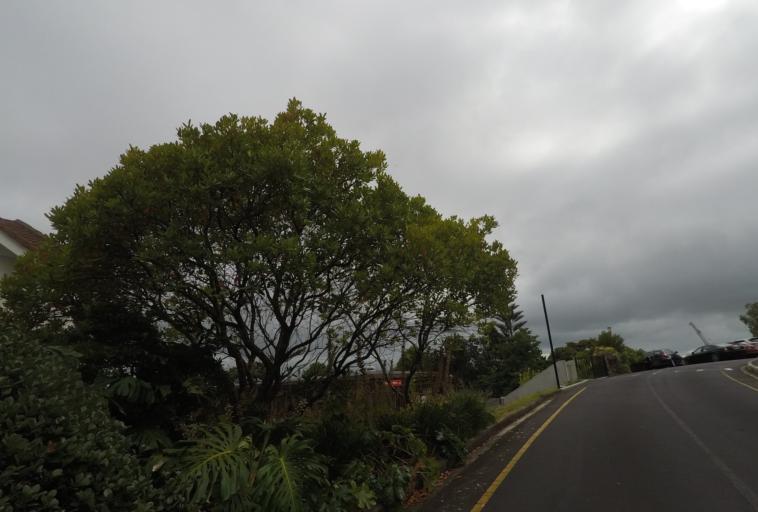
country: NZ
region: Auckland
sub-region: Auckland
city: Auckland
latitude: -36.8732
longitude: 174.7697
